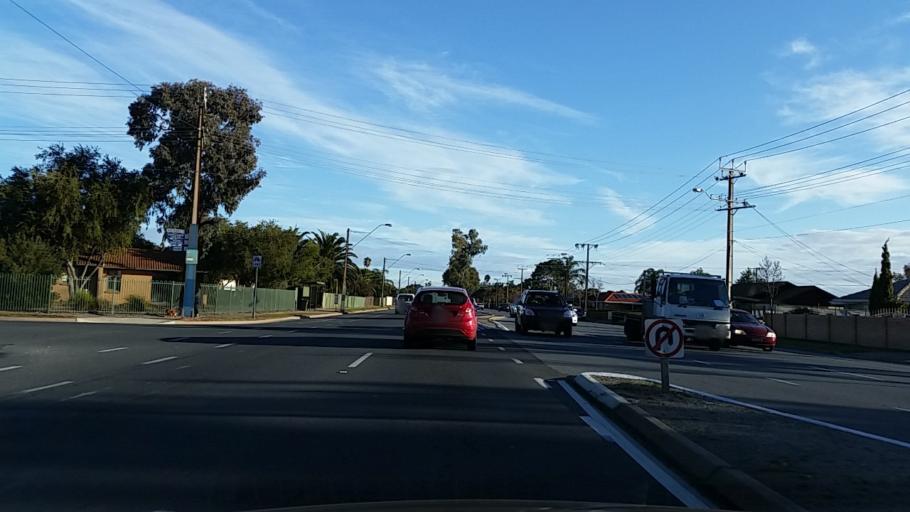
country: AU
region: South Australia
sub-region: Salisbury
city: Salisbury
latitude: -34.7911
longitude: 138.6158
